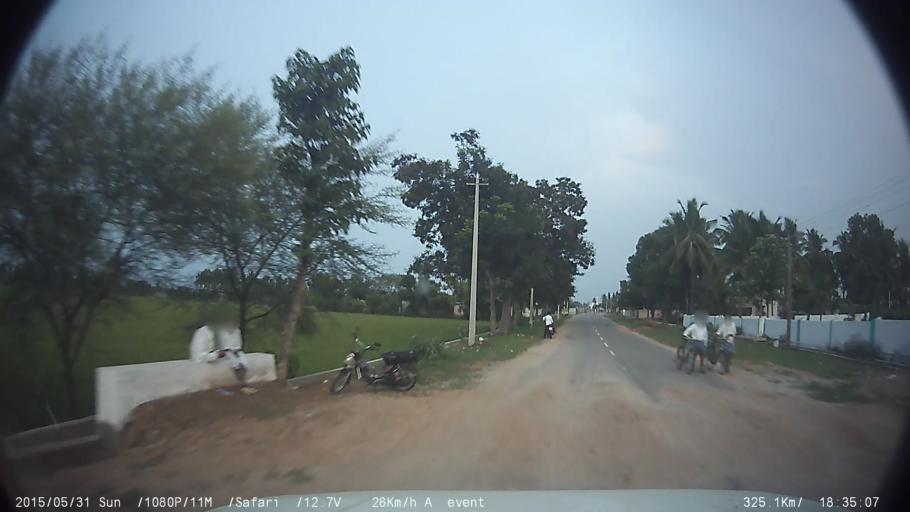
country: IN
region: Karnataka
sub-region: Mysore
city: Nanjangud
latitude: 12.1455
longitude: 76.7596
